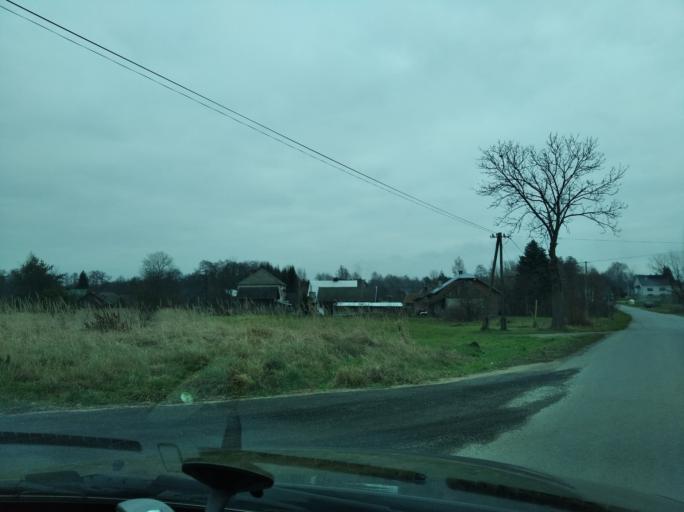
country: PL
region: Subcarpathian Voivodeship
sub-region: Powiat lancucki
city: Brzoza Stadnicka
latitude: 50.2062
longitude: 22.2966
